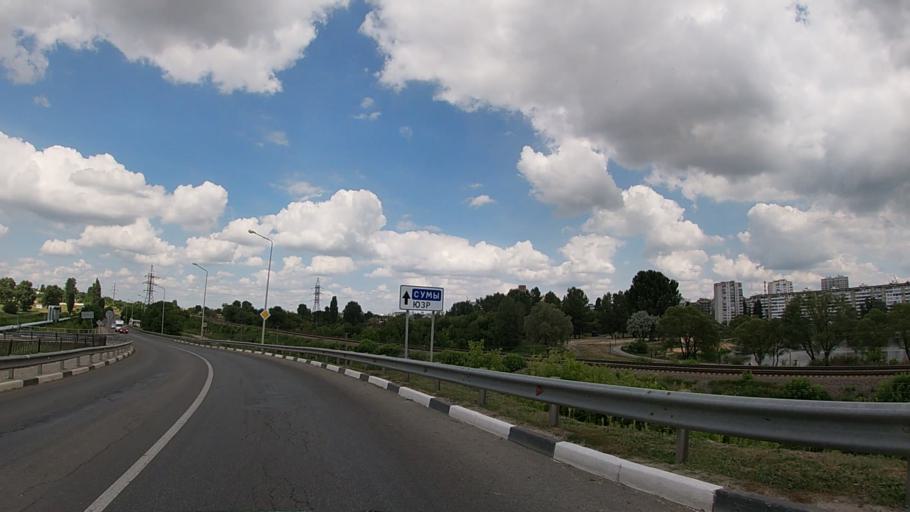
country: RU
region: Belgorod
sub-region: Belgorodskiy Rayon
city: Belgorod
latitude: 50.5909
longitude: 36.5651
